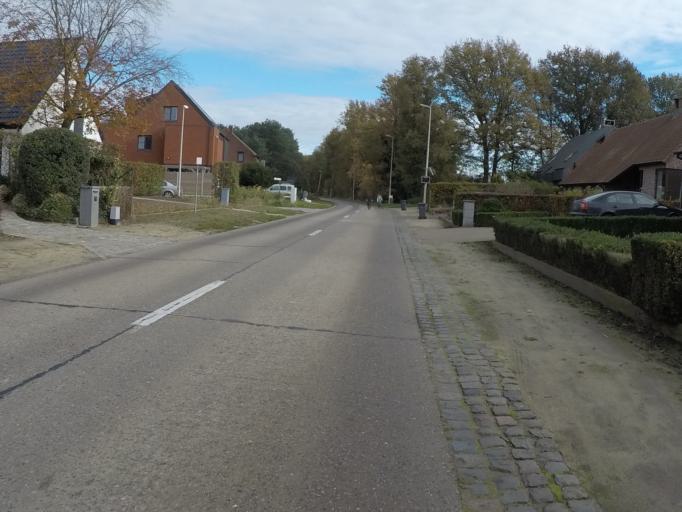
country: BE
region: Flanders
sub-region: Provincie Antwerpen
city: Berlaar
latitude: 51.1424
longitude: 4.6417
